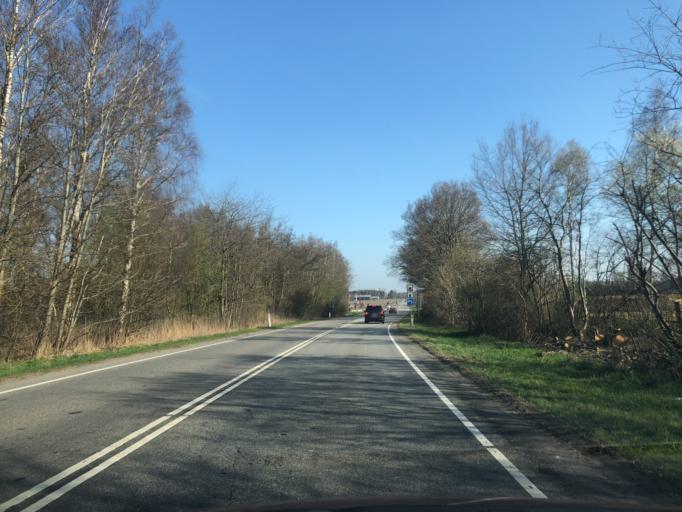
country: DK
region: Zealand
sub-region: Faxe Kommune
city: Haslev
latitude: 55.3263
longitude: 11.9411
